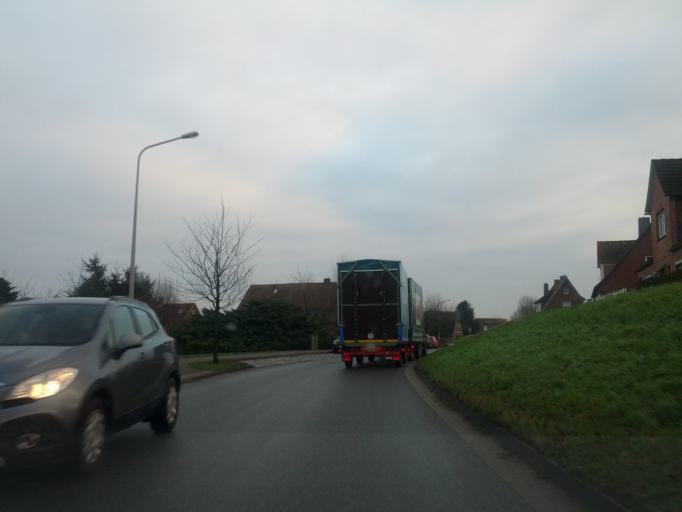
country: DE
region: Lower Saxony
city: Guderhandviertel
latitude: 53.5514
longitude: 9.6096
